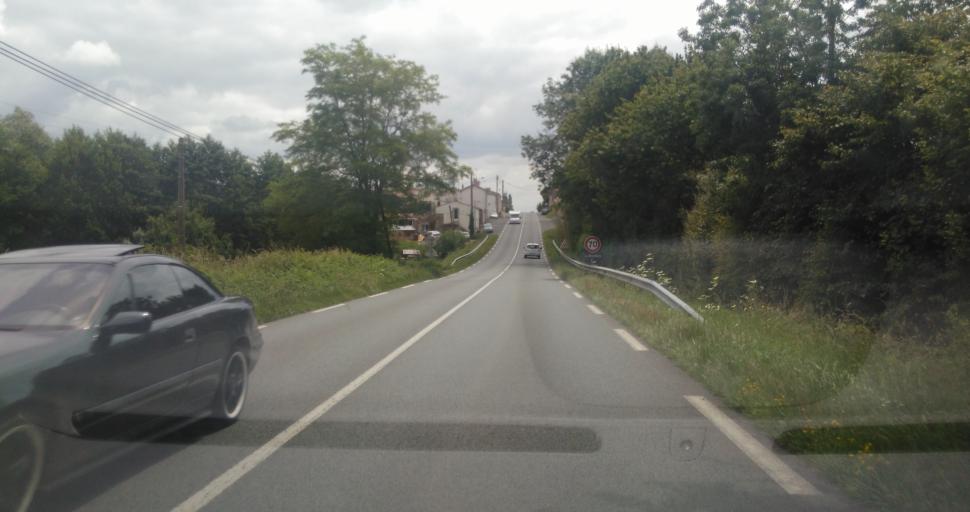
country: FR
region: Pays de la Loire
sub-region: Departement de la Vendee
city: Bournezeau
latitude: 46.6181
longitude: -1.1519
